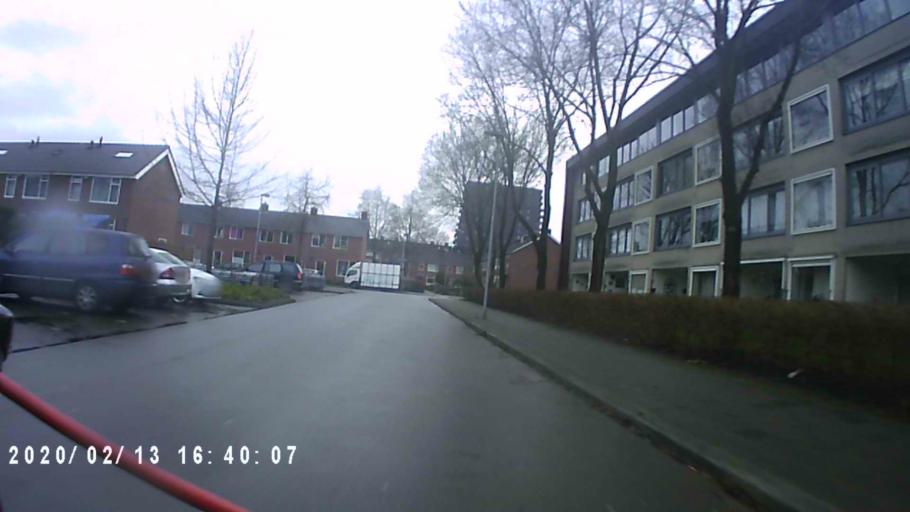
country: NL
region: Groningen
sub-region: Gemeente Groningen
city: Groningen
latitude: 53.2269
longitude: 6.5228
